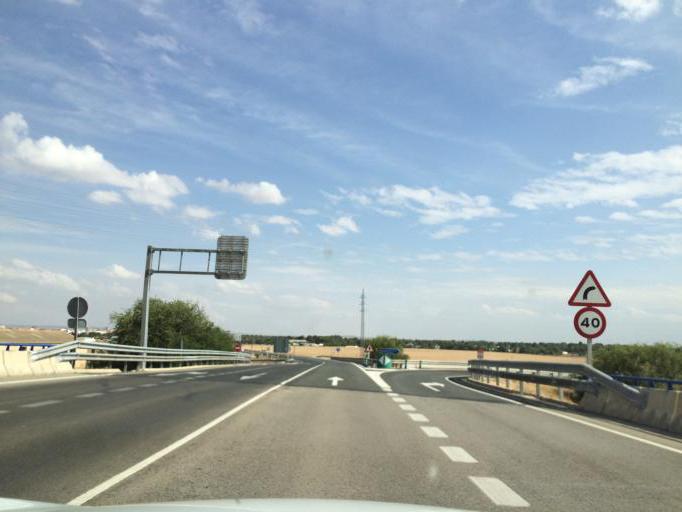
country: ES
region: Castille-La Mancha
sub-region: Provincia de Albacete
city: Albacete
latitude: 39.0018
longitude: -1.9029
